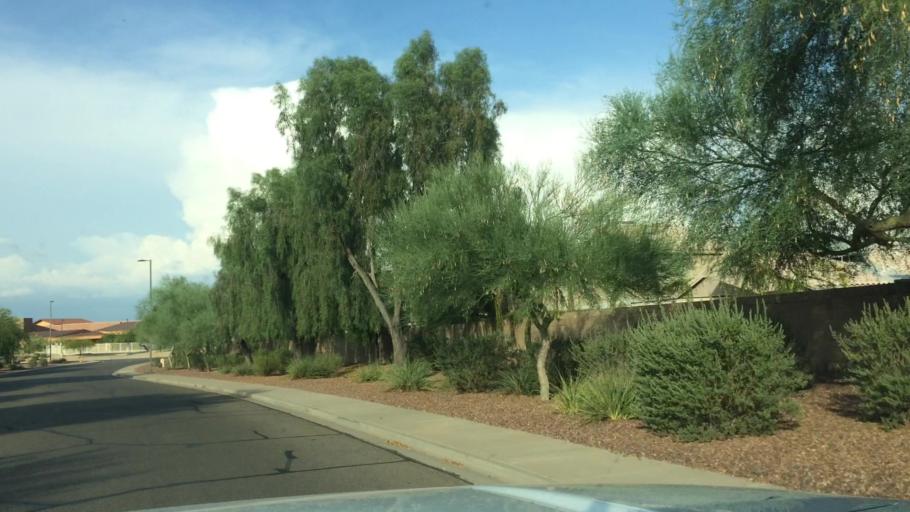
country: US
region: Arizona
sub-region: Maricopa County
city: Cave Creek
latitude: 33.6919
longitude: -112.0377
